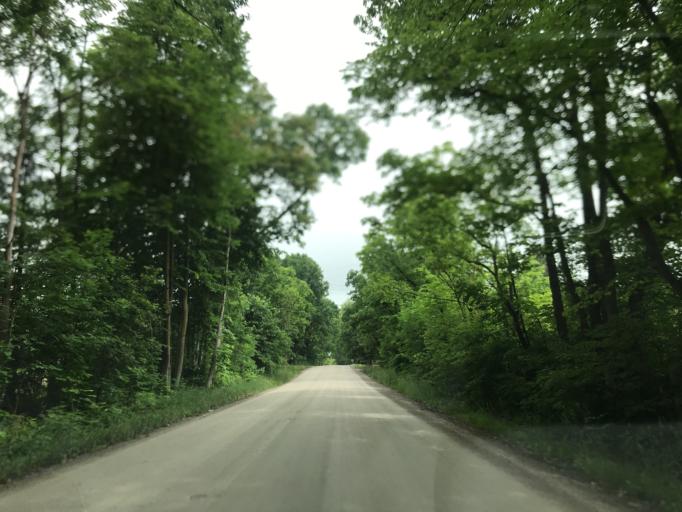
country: US
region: Michigan
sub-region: Oakland County
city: South Lyon
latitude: 42.4250
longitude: -83.6257
